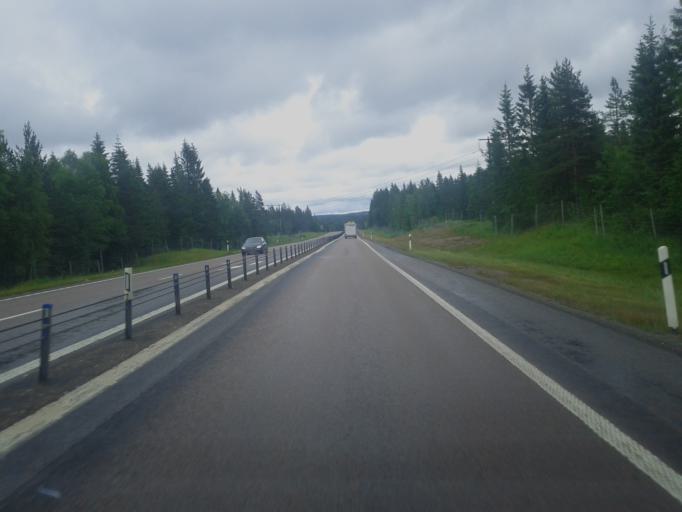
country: SE
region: Vaesternorrland
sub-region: Timra Kommun
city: Soraker
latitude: 62.5344
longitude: 17.5186
